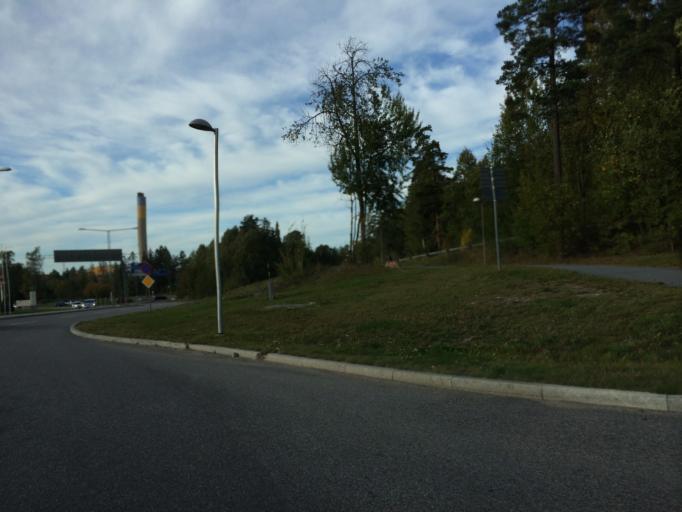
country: SE
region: Stockholm
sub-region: Stockholms Kommun
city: Kista
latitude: 59.4128
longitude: 17.9329
